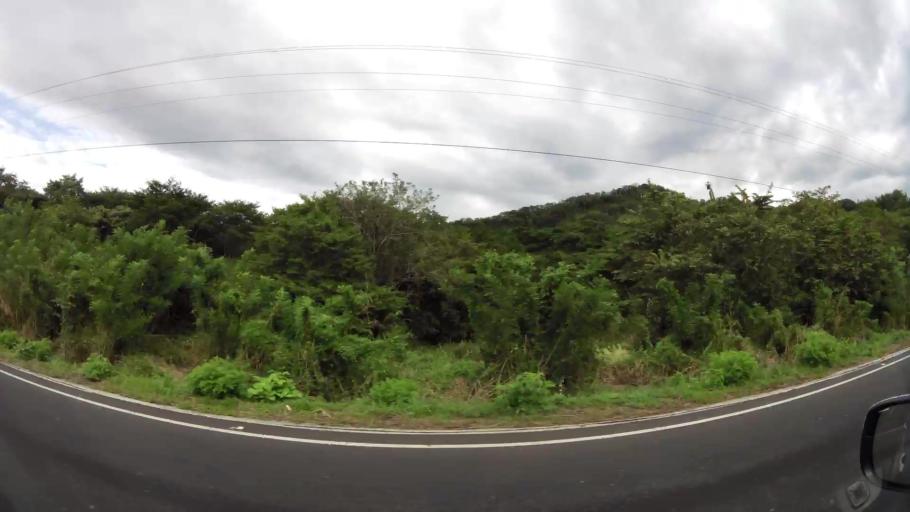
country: CR
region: Guanacaste
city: Nandayure
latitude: 10.2450
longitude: -85.2239
